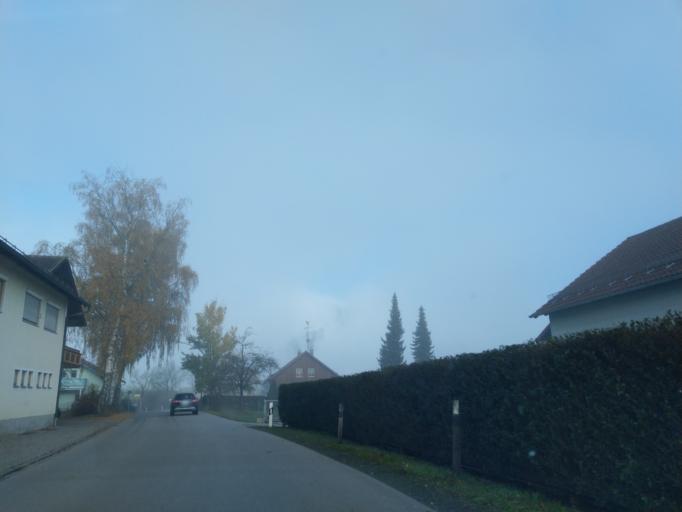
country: DE
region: Bavaria
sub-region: Lower Bavaria
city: Aussernzell
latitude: 48.7255
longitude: 13.2045
